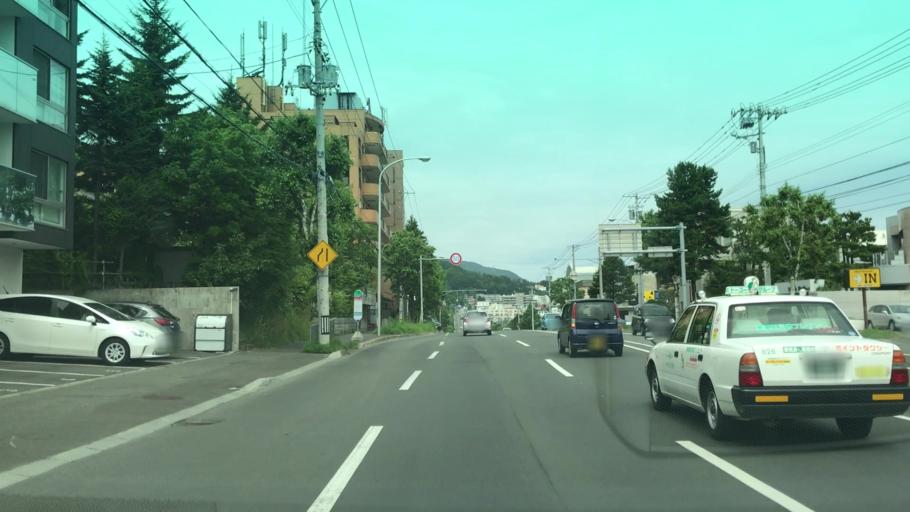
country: JP
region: Hokkaido
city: Sapporo
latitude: 43.0589
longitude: 141.2998
